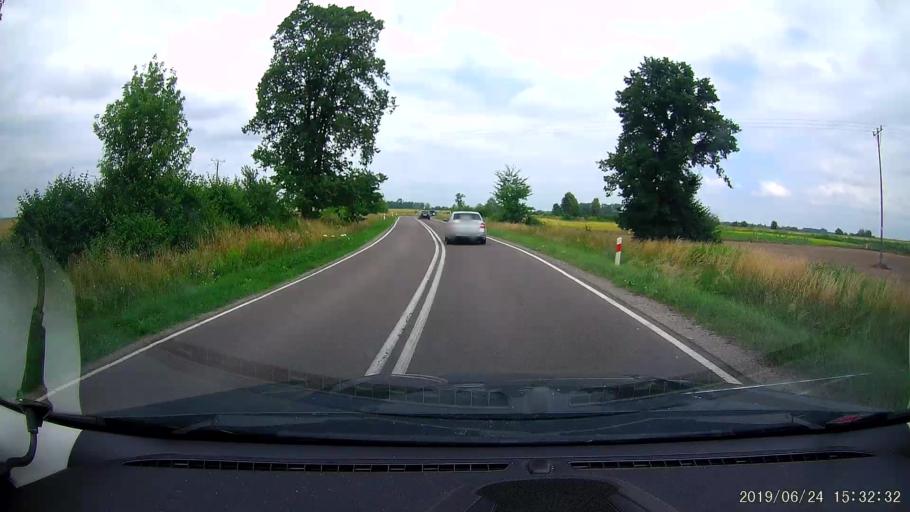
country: PL
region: Subcarpathian Voivodeship
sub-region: Powiat jaroslawski
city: Wiazownica
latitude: 50.0407
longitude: 22.7569
